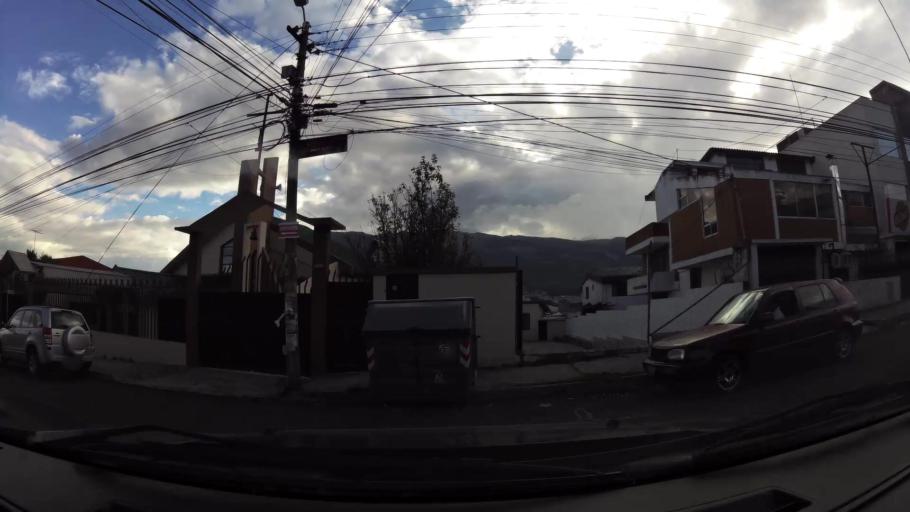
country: EC
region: Pichincha
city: Quito
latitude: -0.1343
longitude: -78.4806
